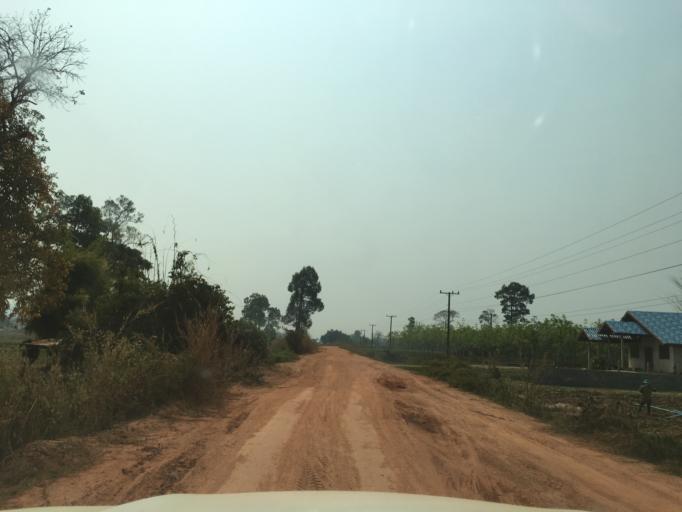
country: TH
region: Changwat Bueng Kan
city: Bung Khla
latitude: 18.2084
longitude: 104.0738
